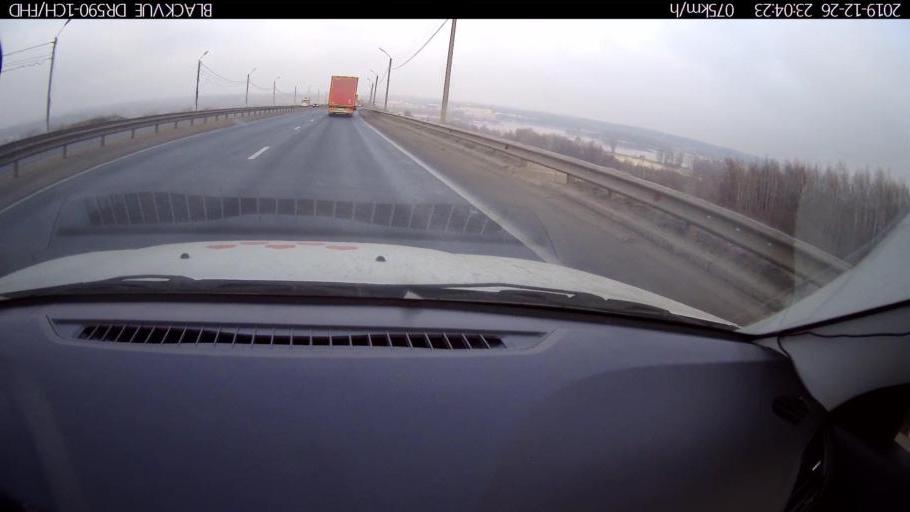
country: RU
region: Nizjnij Novgorod
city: Burevestnik
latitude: 56.1794
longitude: 43.7482
